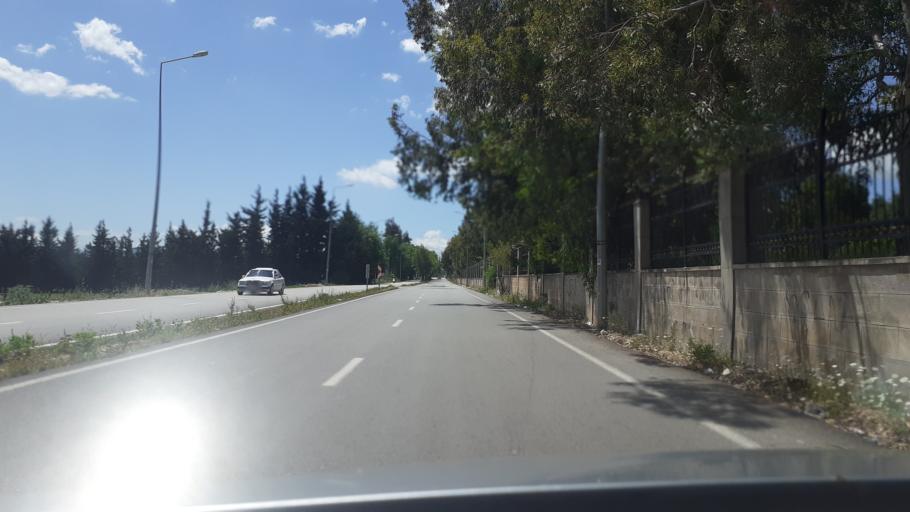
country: TR
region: Hatay
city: Anayazi
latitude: 36.3249
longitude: 36.1983
